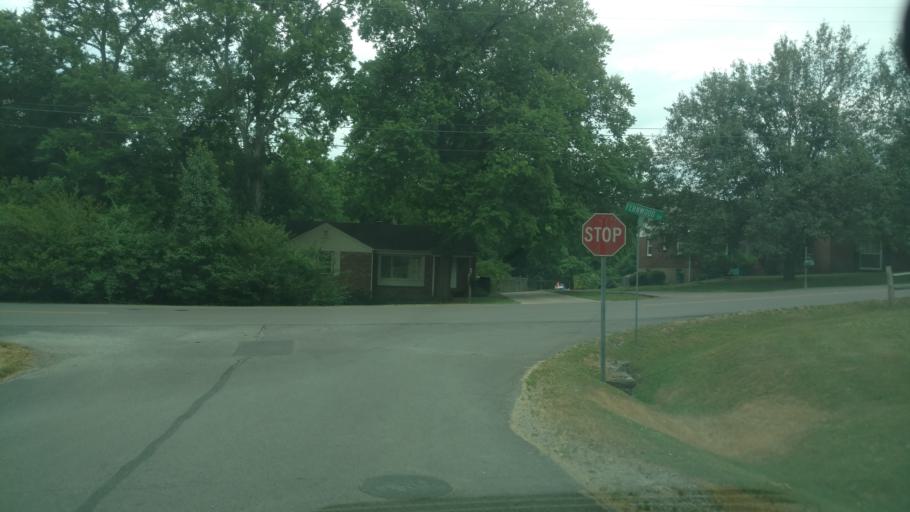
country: US
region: Tennessee
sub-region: Davidson County
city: Nashville
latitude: 36.2031
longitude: -86.7121
